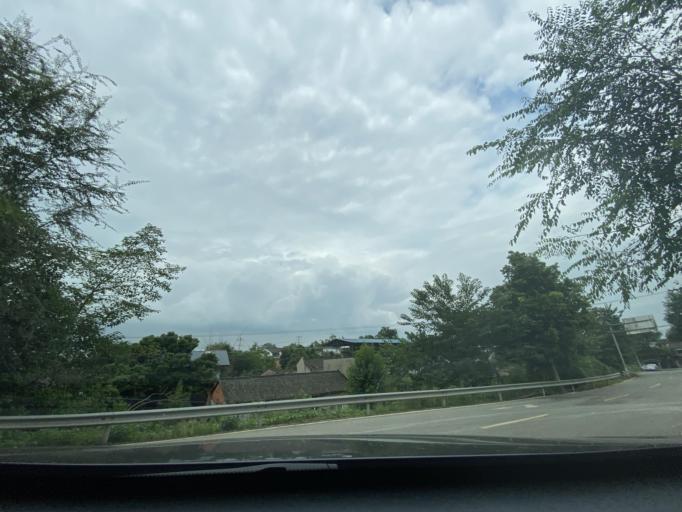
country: CN
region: Sichuan
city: Wujin
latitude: 30.3700
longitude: 103.9677
